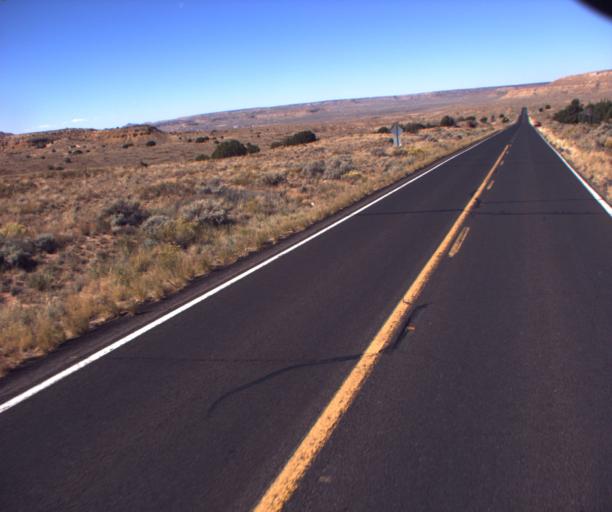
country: US
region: Arizona
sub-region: Navajo County
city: First Mesa
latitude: 35.8639
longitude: -110.5408
